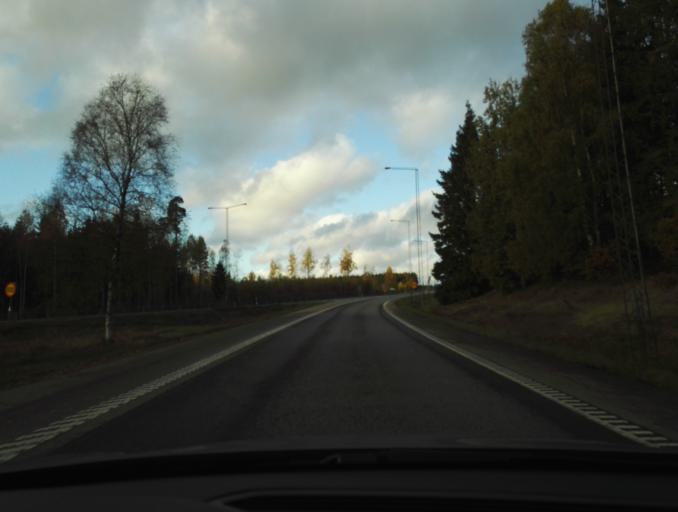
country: SE
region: Kronoberg
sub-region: Vaxjo Kommun
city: Vaexjoe
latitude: 56.8987
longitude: 14.7303
